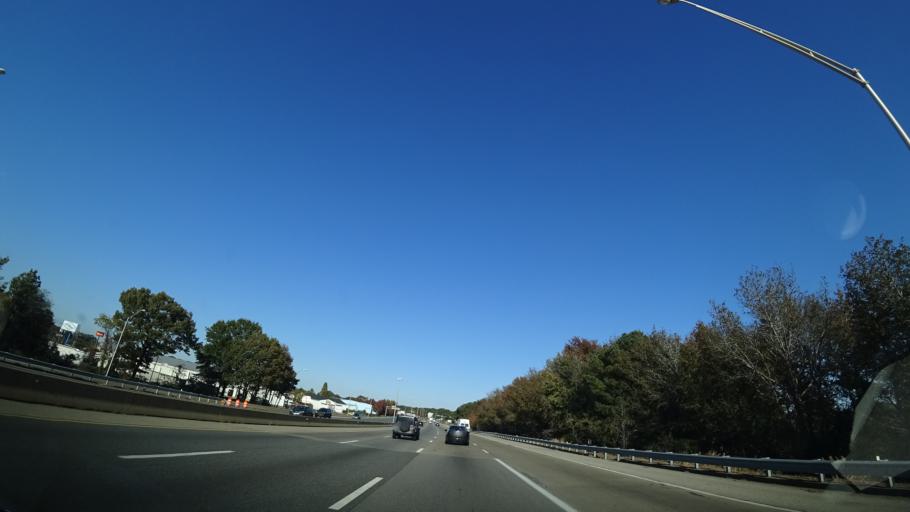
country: US
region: Virginia
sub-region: City of Newport News
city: Newport News
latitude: 37.0054
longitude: -76.4015
